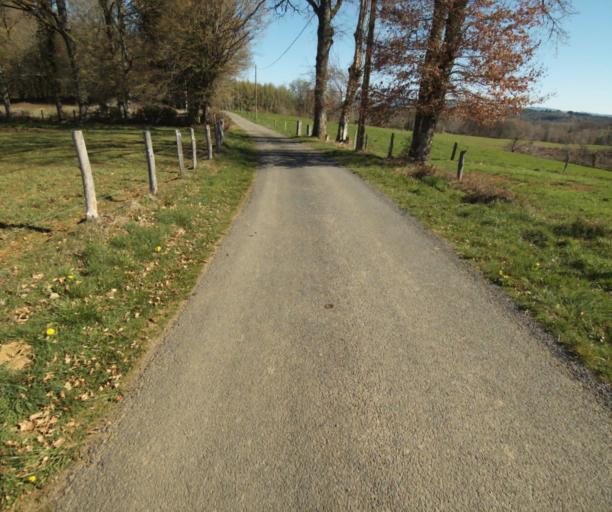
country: FR
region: Limousin
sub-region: Departement de la Correze
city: Seilhac
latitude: 45.3981
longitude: 1.7331
